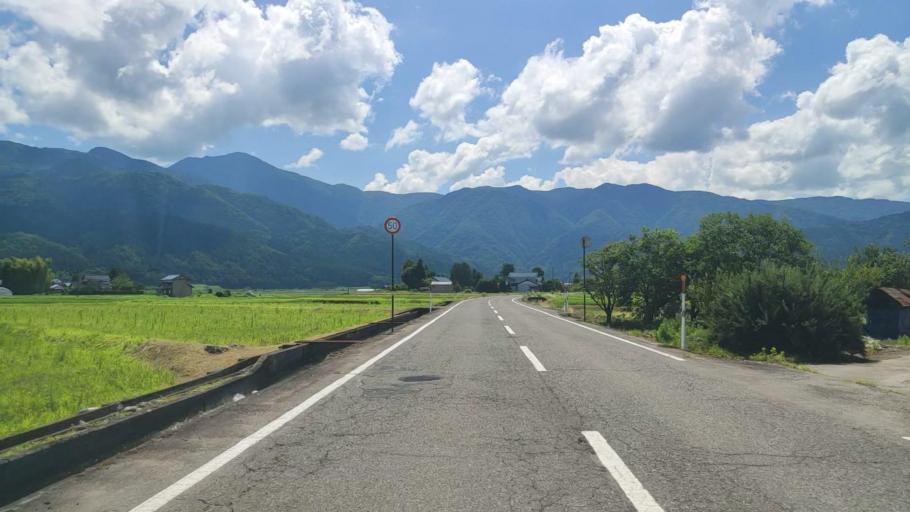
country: JP
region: Fukui
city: Ono
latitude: 35.9586
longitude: 136.5348
